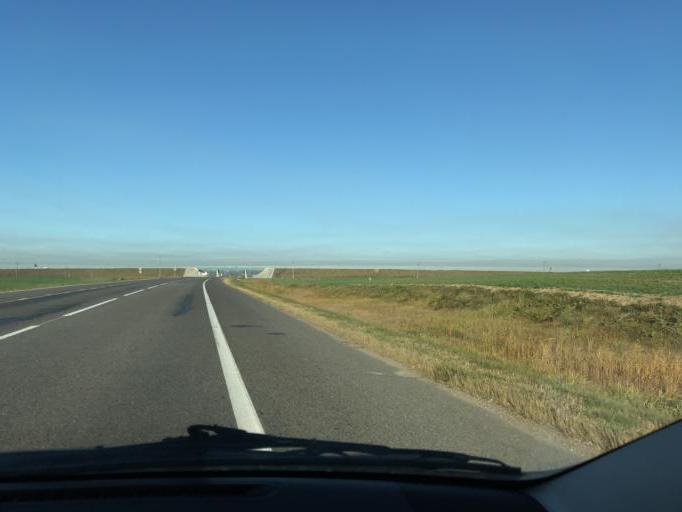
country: BY
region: Vitebsk
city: Vitebsk
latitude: 55.1077
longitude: 30.1102
